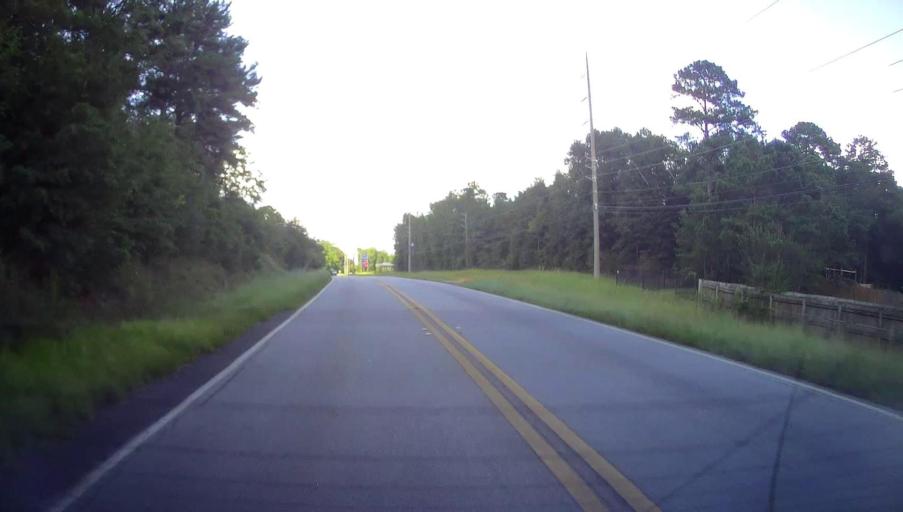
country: US
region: Georgia
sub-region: Muscogee County
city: Columbus
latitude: 32.5418
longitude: -84.8961
